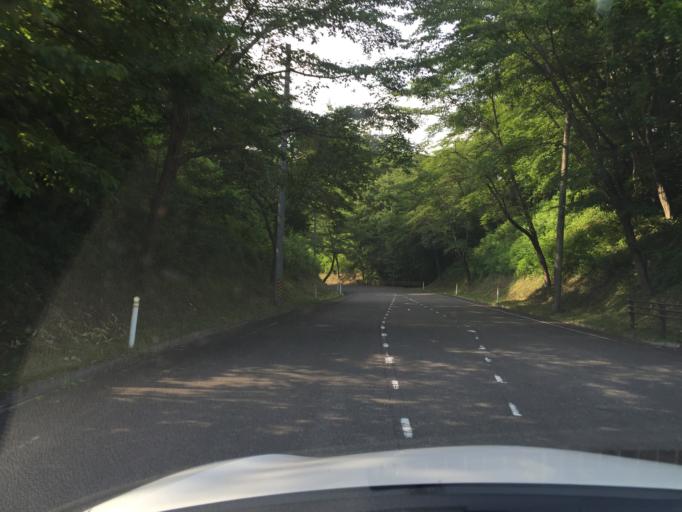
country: JP
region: Fukushima
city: Miharu
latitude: 37.3978
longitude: 140.4803
